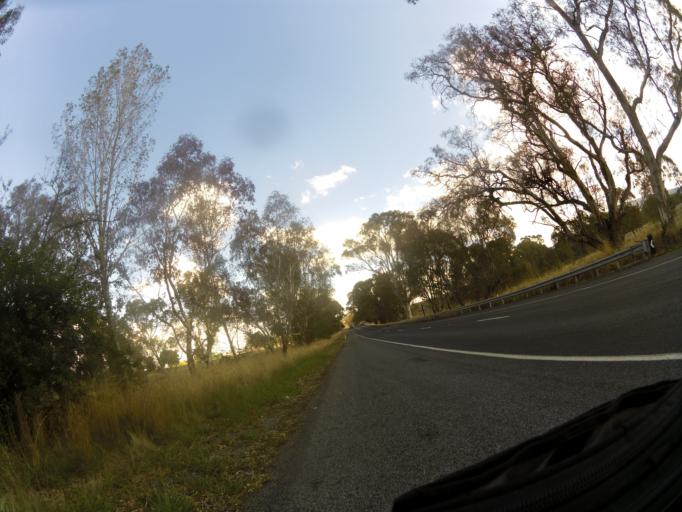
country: AU
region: Victoria
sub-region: Mansfield
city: Mansfield
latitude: -36.9344
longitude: 145.9998
